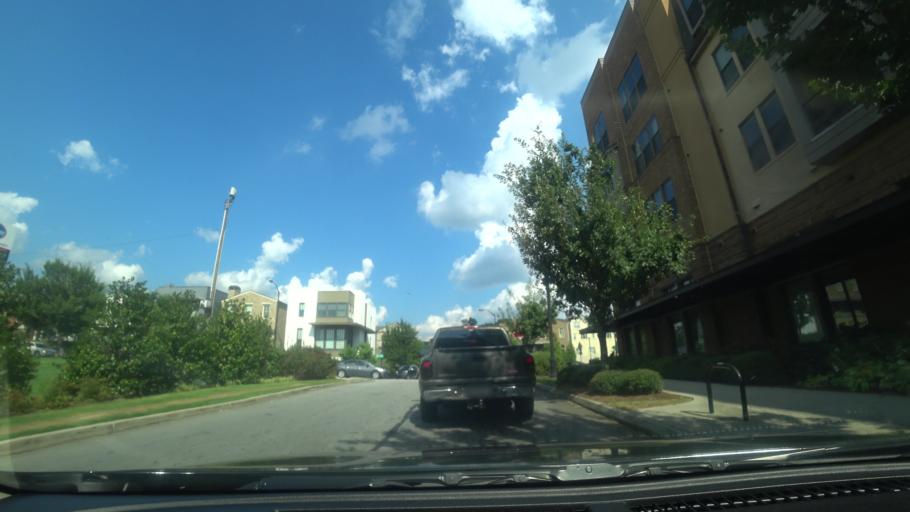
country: US
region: Georgia
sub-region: Fulton County
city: Atlanta
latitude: 33.7455
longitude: -84.3585
